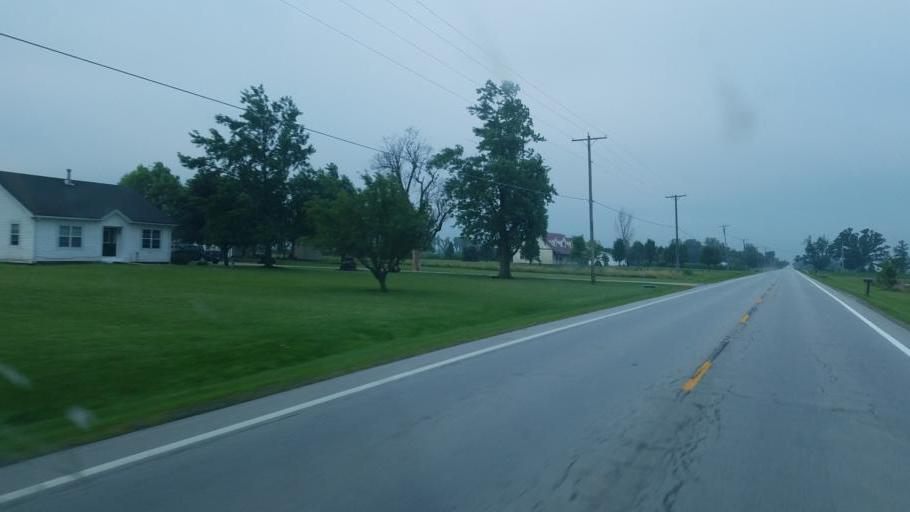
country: US
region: Ohio
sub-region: Madison County
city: Bethel
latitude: 39.6367
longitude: -83.3436
